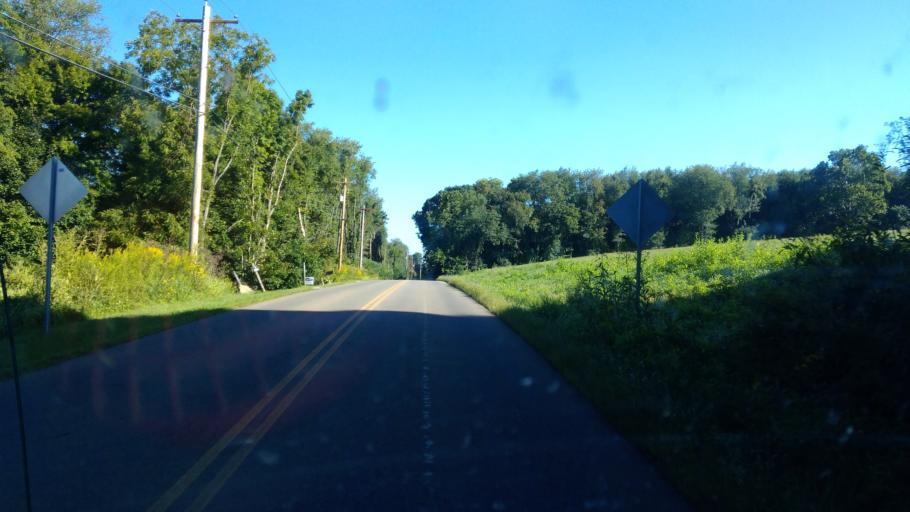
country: US
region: Ohio
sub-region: Knox County
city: Gambier
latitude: 40.4119
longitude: -82.3687
